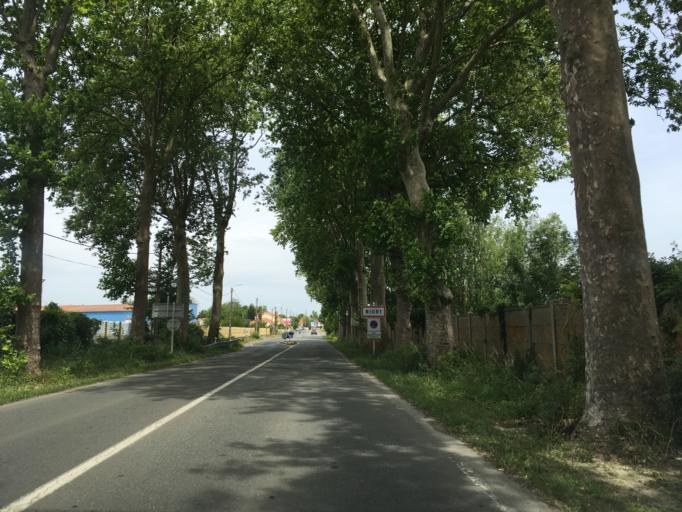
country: FR
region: Poitou-Charentes
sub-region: Departement des Deux-Sevres
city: Niort
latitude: 46.3010
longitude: -0.4658
